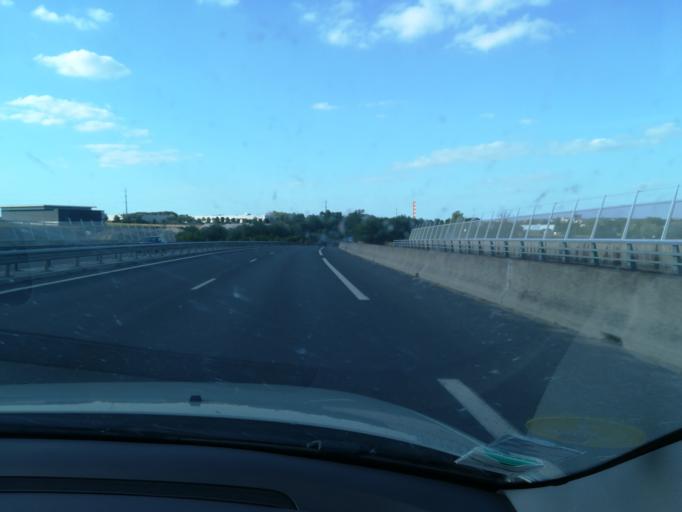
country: FR
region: Champagne-Ardenne
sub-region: Departement de la Marne
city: Bezannes
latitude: 49.2076
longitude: 4.0121
